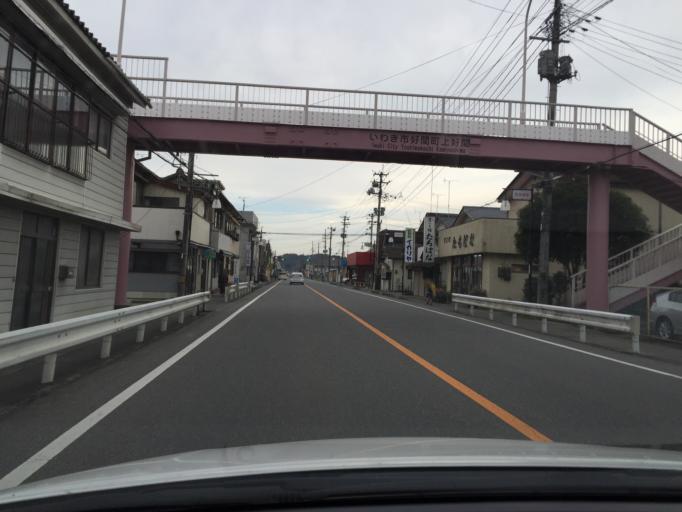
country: JP
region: Fukushima
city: Iwaki
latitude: 37.0667
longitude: 140.8501
